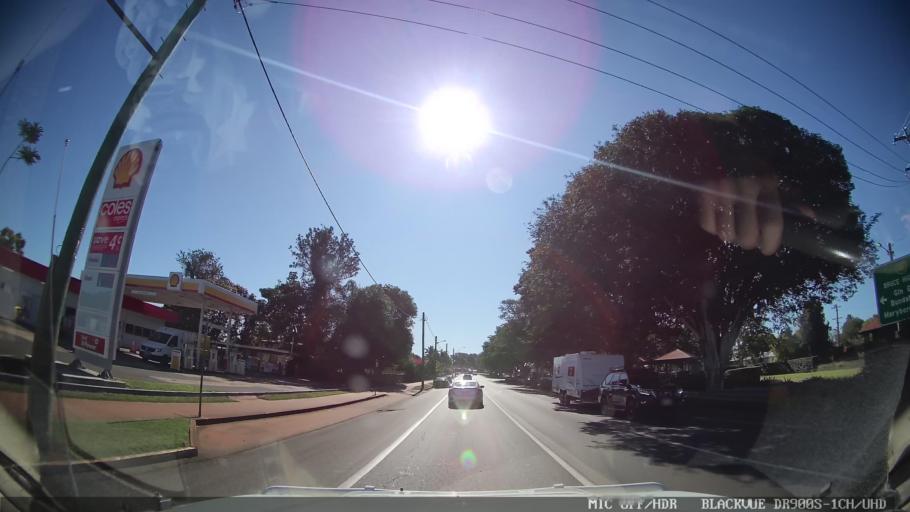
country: AU
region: Queensland
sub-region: Bundaberg
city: Childers
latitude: -25.2354
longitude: 152.2747
